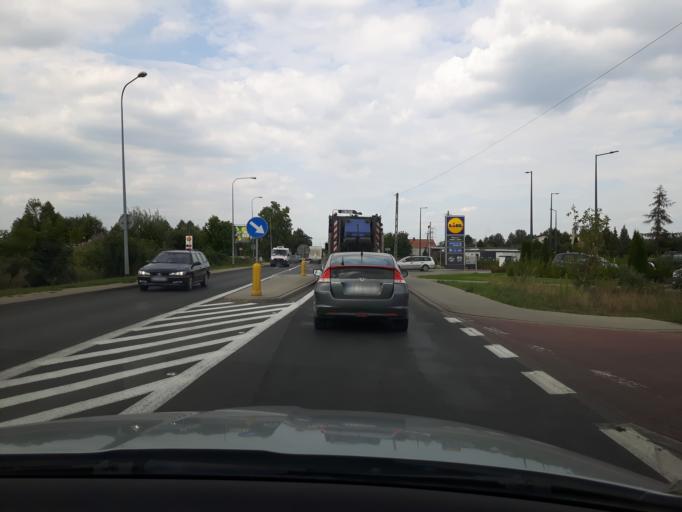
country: PL
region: Masovian Voivodeship
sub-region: Powiat legionowski
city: Stanislawow Pierwszy
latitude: 52.3633
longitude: 21.0280
